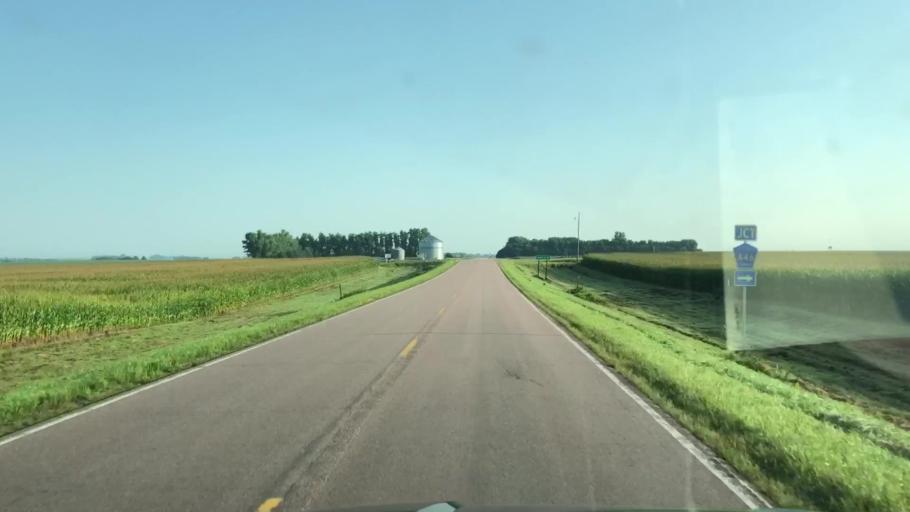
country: US
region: Iowa
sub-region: Lyon County
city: George
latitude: 43.3148
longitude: -95.9990
